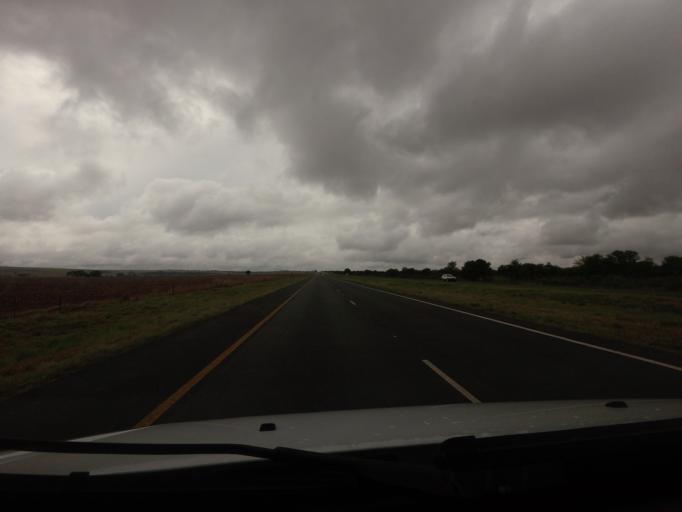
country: ZA
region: Mpumalanga
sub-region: Nkangala District Municipality
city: Witbank
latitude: -25.8695
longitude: 29.0213
